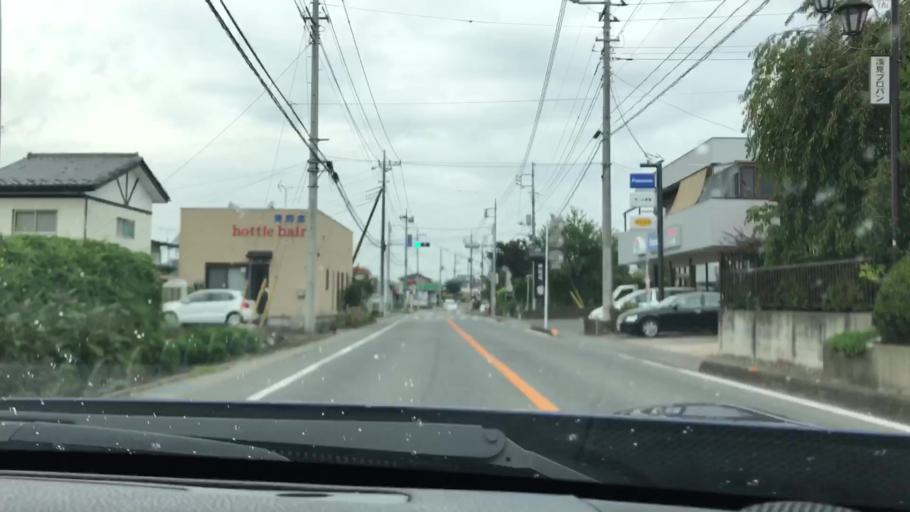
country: JP
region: Gunma
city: Kanekomachi
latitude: 36.3970
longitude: 138.9689
